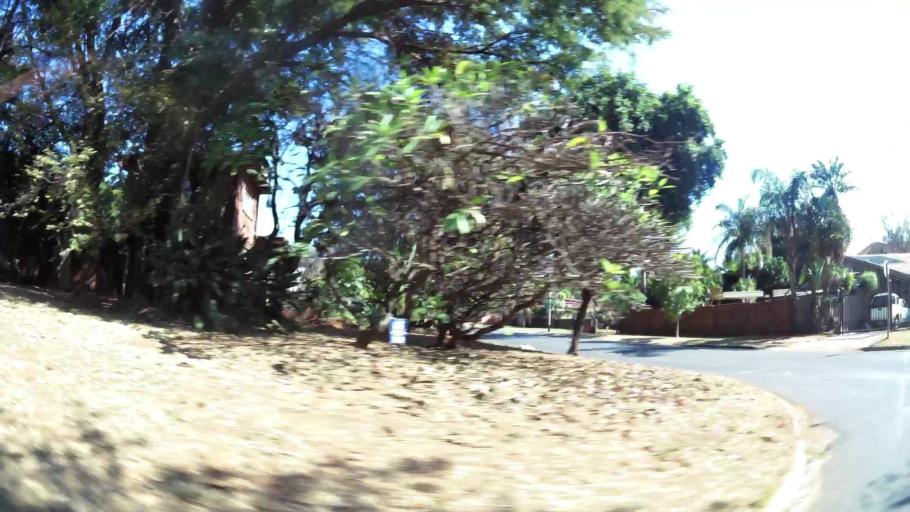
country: ZA
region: Gauteng
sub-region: City of Tshwane Metropolitan Municipality
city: Pretoria
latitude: -25.6884
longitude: 28.2252
